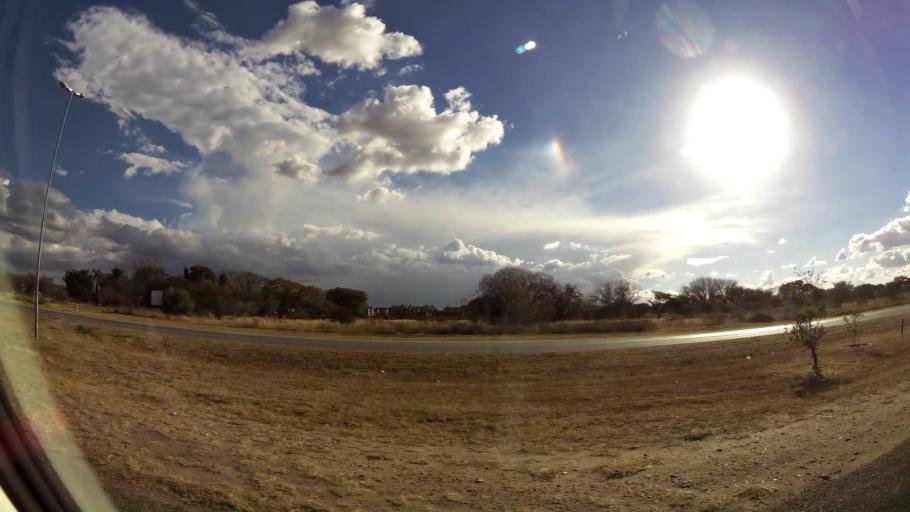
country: ZA
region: Limpopo
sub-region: Capricorn District Municipality
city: Polokwane
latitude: -23.9373
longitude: 29.4491
